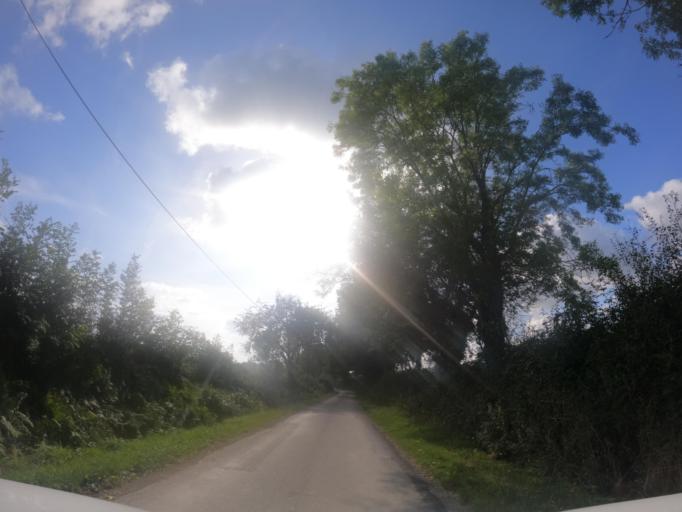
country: FR
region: Poitou-Charentes
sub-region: Departement des Deux-Sevres
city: Courlay
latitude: 46.7765
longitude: -0.5982
